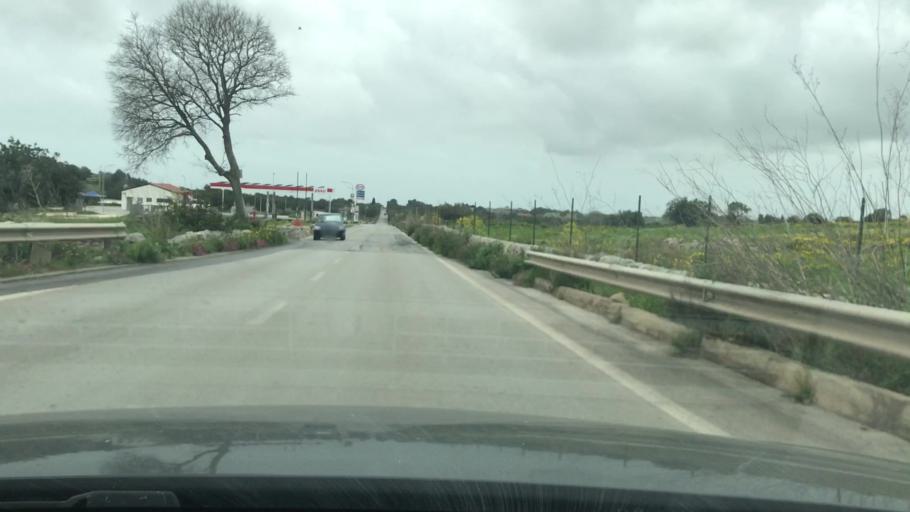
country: IT
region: Sicily
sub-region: Ragusa
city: Scicli
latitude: 36.8142
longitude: 14.7329
